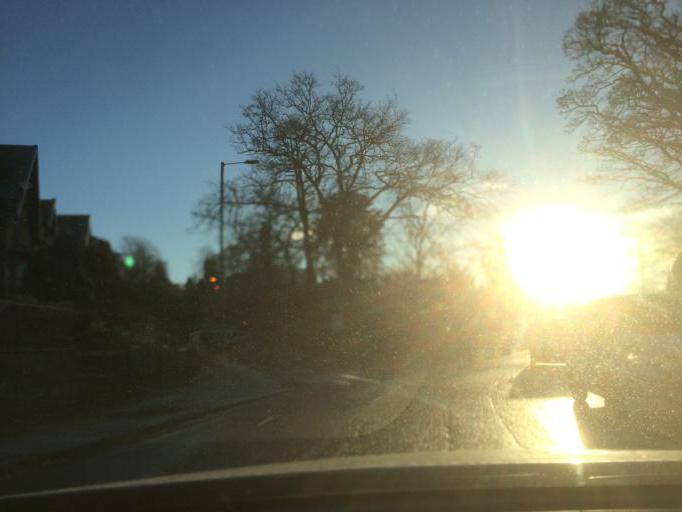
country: GB
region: Scotland
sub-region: East Renfrewshire
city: Giffnock
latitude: 55.8171
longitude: -4.3025
